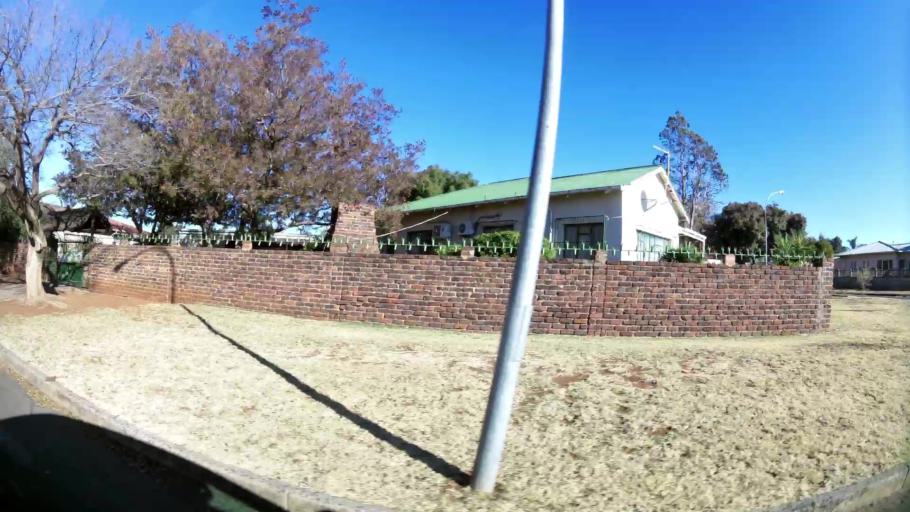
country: ZA
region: Northern Cape
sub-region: Frances Baard District Municipality
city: Kimberley
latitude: -28.7511
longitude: 24.7903
